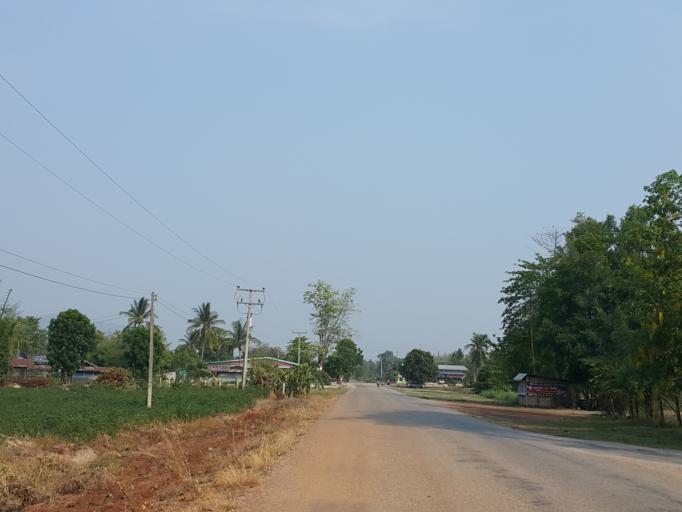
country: TH
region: Uthai Thani
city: Lan Sak
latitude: 15.3926
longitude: 99.5725
